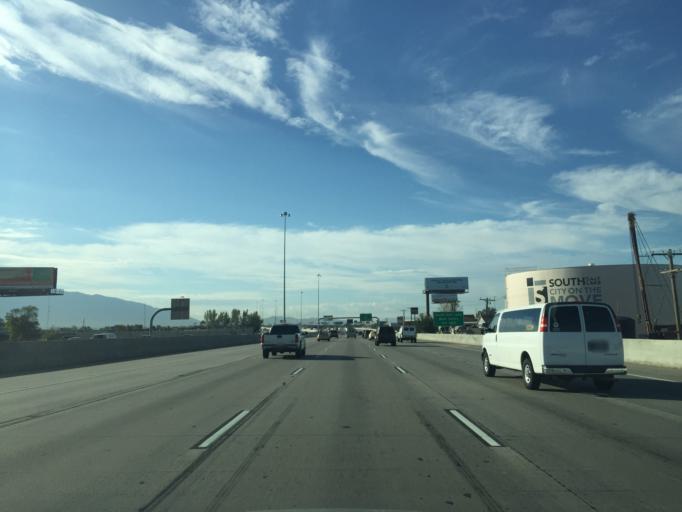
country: US
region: Utah
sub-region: Salt Lake County
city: Centerfield
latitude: 40.7075
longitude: -111.9039
